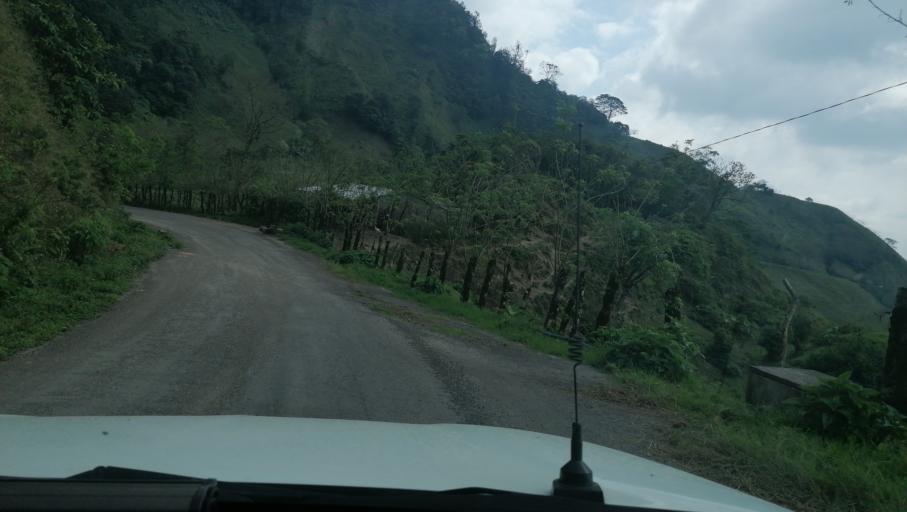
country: MX
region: Chiapas
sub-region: Francisco Leon
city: San Miguel la Sardina
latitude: 17.2419
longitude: -93.2994
